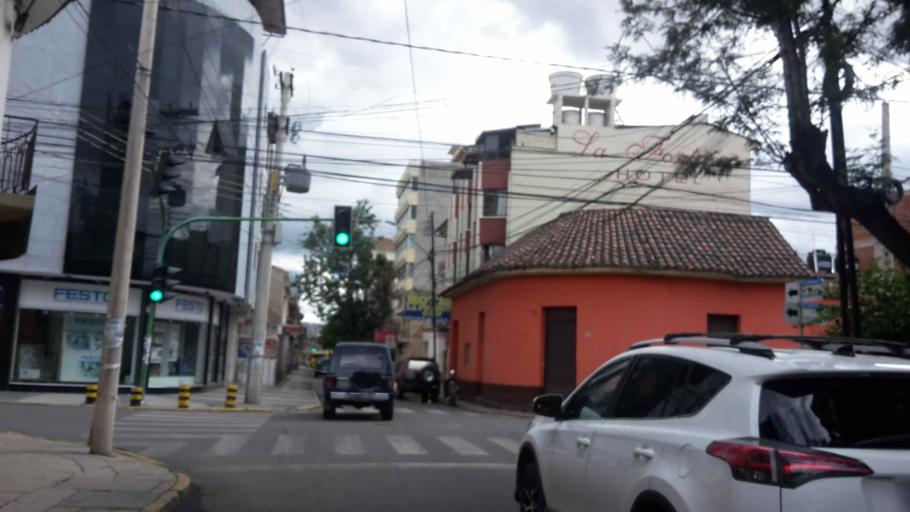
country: BO
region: Cochabamba
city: Cochabamba
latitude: -17.3914
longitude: -66.1610
